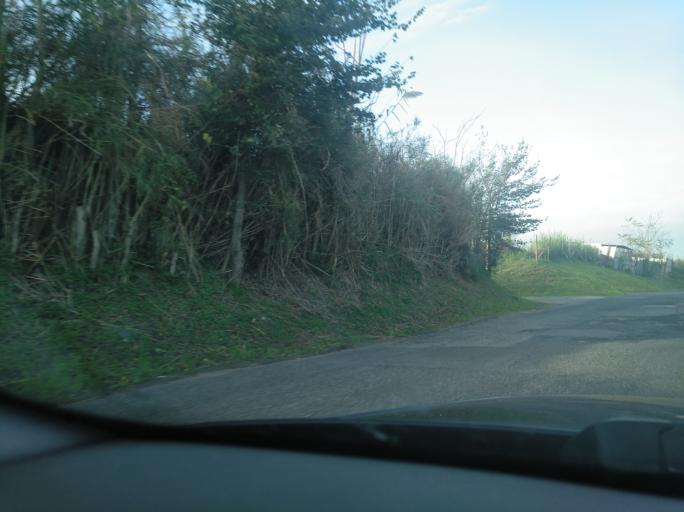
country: PT
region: Lisbon
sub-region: Odivelas
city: Pontinha
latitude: 38.7734
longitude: -9.1892
